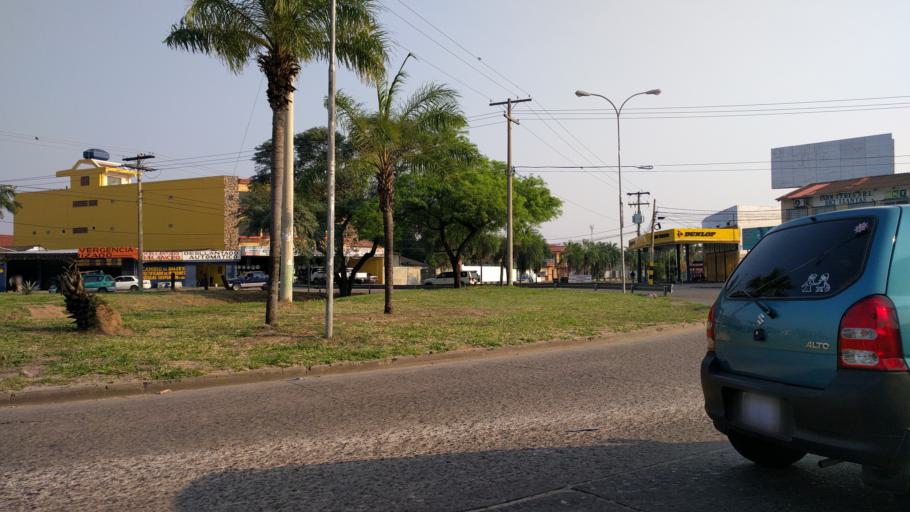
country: BO
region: Santa Cruz
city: Santa Cruz de la Sierra
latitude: -17.7904
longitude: -63.2064
